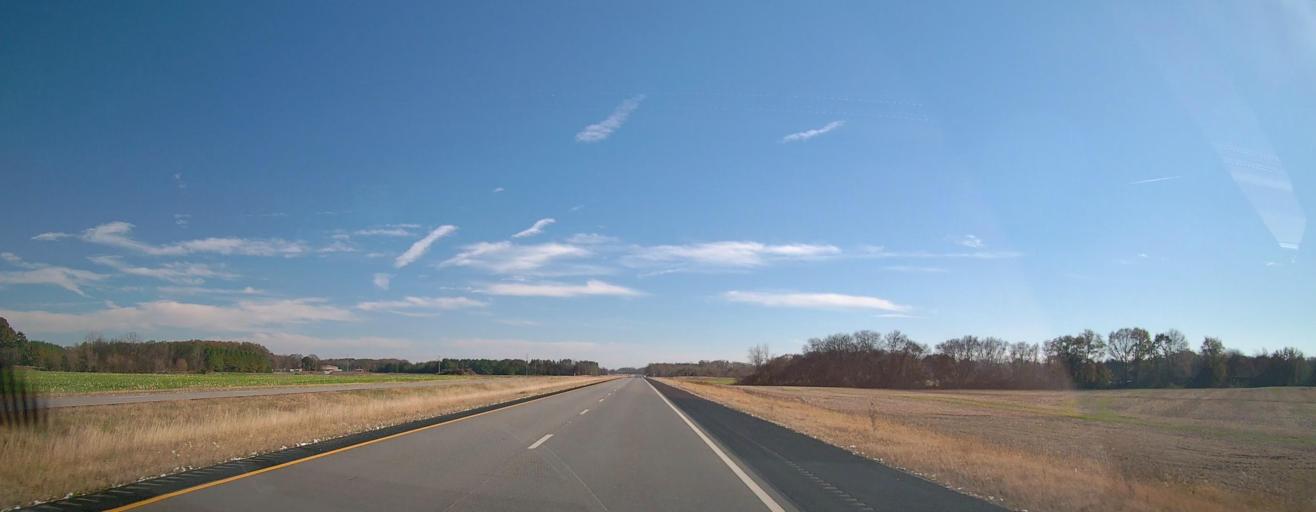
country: US
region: Alabama
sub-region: Lawrence County
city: Town Creek
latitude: 34.6806
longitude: -87.3011
